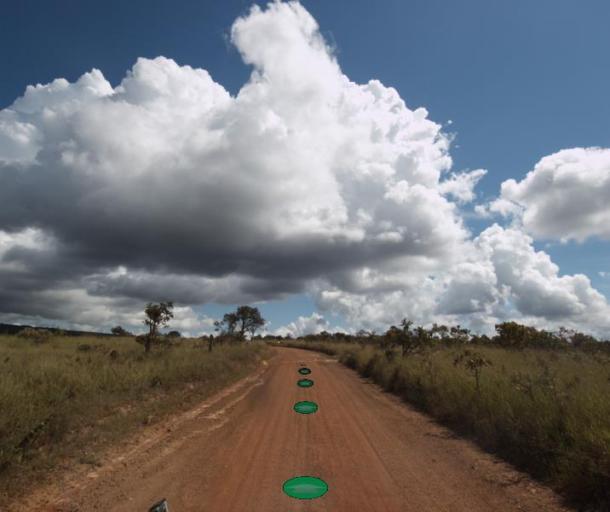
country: BR
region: Goias
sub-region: Pirenopolis
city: Pirenopolis
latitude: -15.7804
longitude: -48.8589
